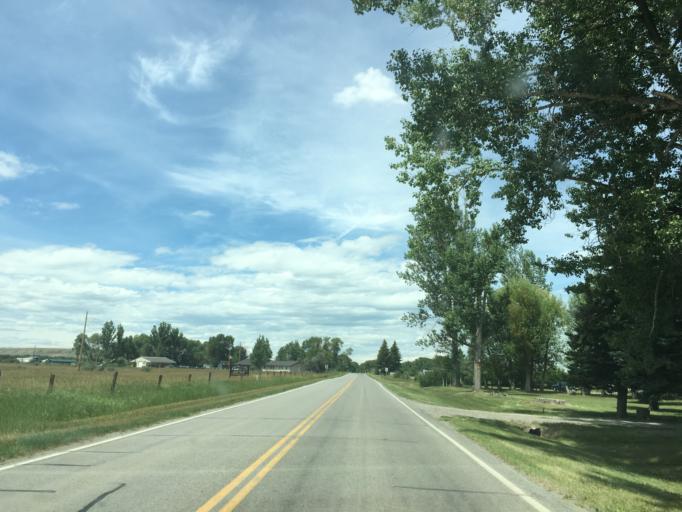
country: US
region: Montana
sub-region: Teton County
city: Choteau
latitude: 47.8255
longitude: -112.1941
